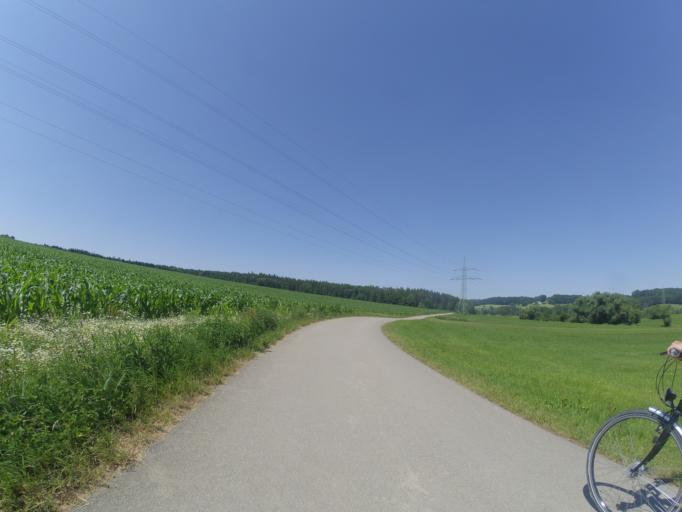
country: DE
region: Bavaria
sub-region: Swabia
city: Ottobeuren
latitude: 47.9514
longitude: 10.2904
